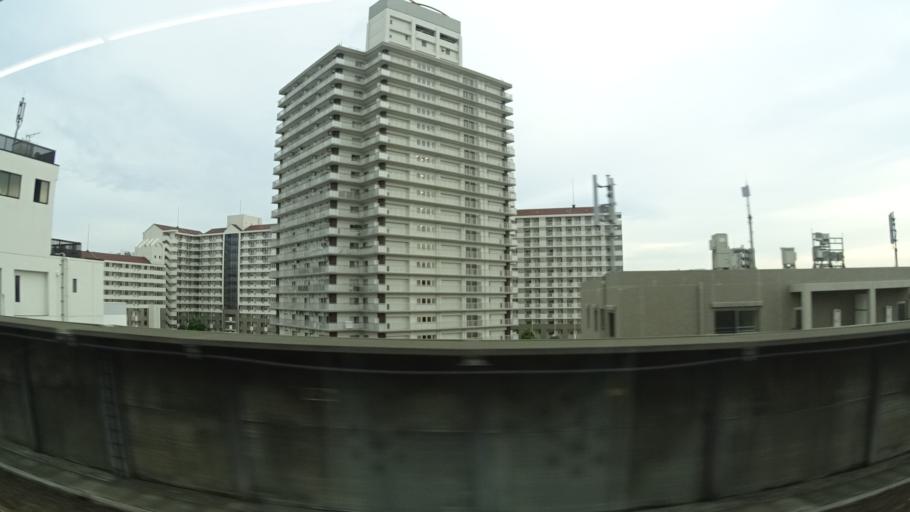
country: JP
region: Saitama
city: Kawaguchi
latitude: 35.7880
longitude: 139.7041
